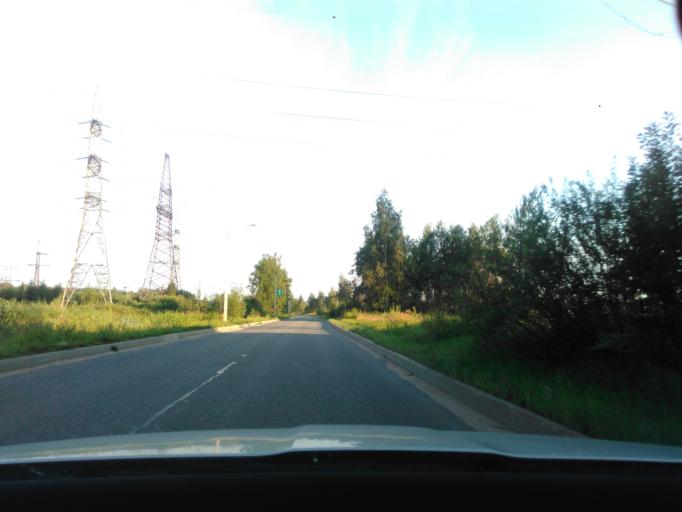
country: RU
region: Tverskaya
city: Konakovo
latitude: 56.7420
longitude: 36.7791
